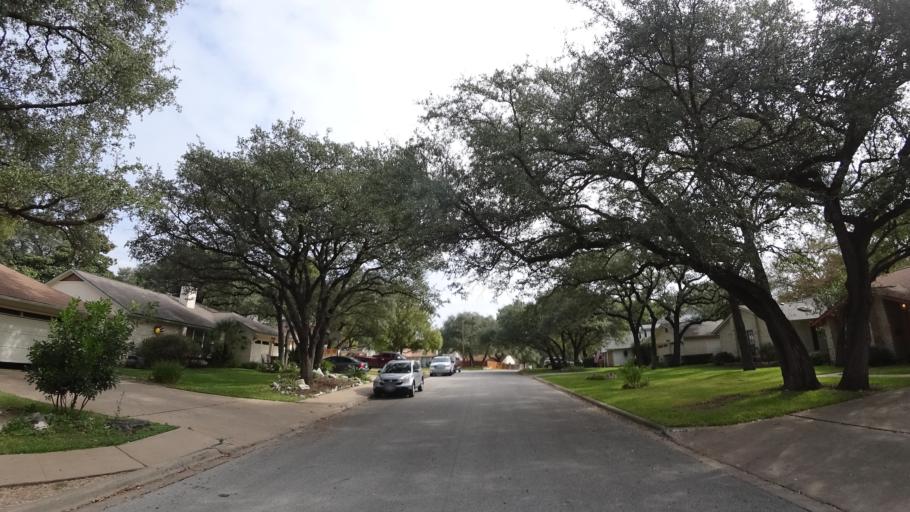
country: US
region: Texas
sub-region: Travis County
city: Wells Branch
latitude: 30.4268
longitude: -97.7076
